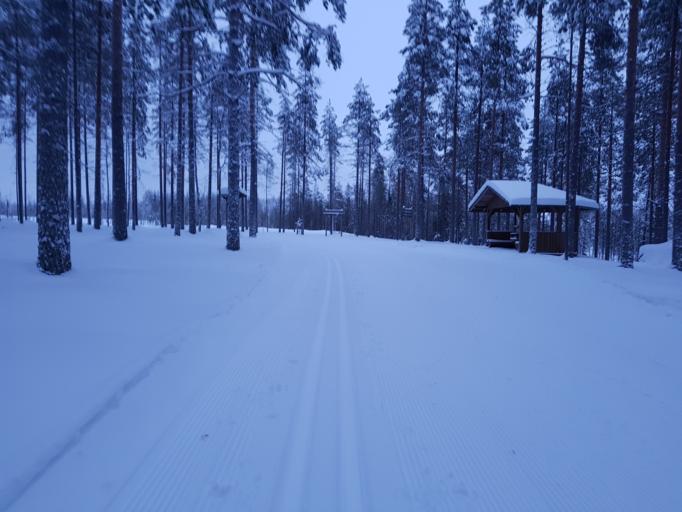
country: FI
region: Kainuu
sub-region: Kehys-Kainuu
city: Kuhmo
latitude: 64.0840
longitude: 29.5240
